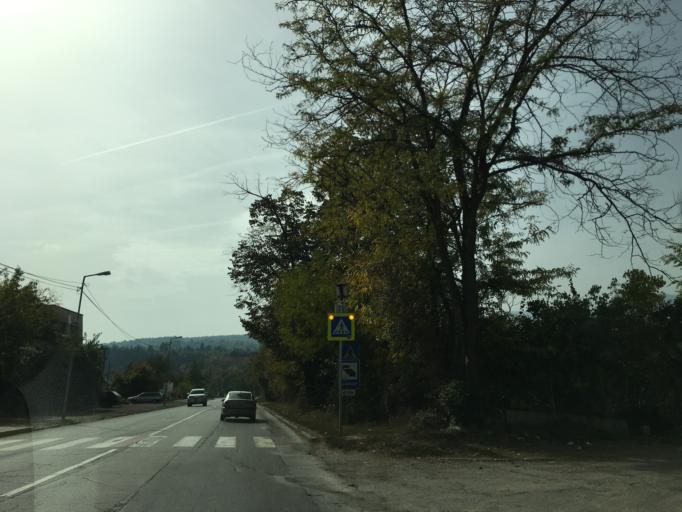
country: BG
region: Sofia-Capital
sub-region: Stolichna Obshtina
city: Sofia
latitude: 42.6153
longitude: 23.4010
